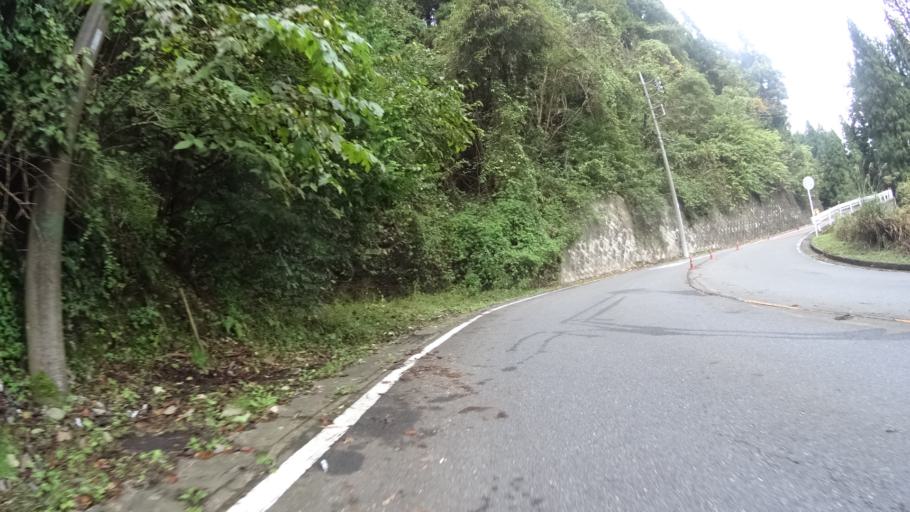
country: JP
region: Yamanashi
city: Uenohara
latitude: 35.6983
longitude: 139.1055
